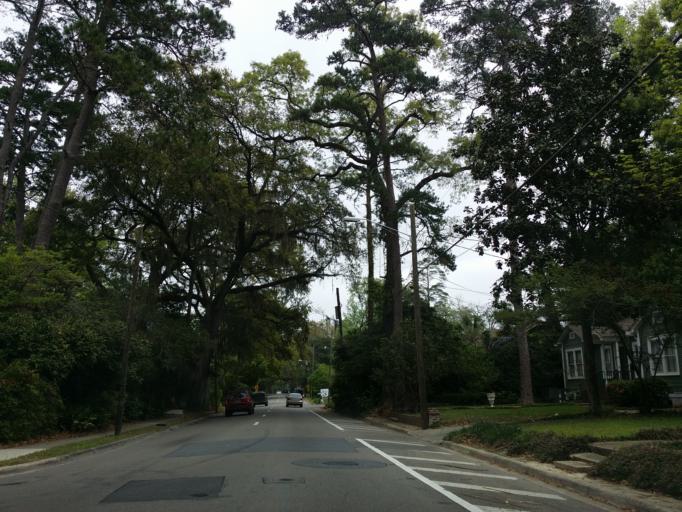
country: US
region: Florida
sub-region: Leon County
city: Tallahassee
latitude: 30.4563
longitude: -84.2725
